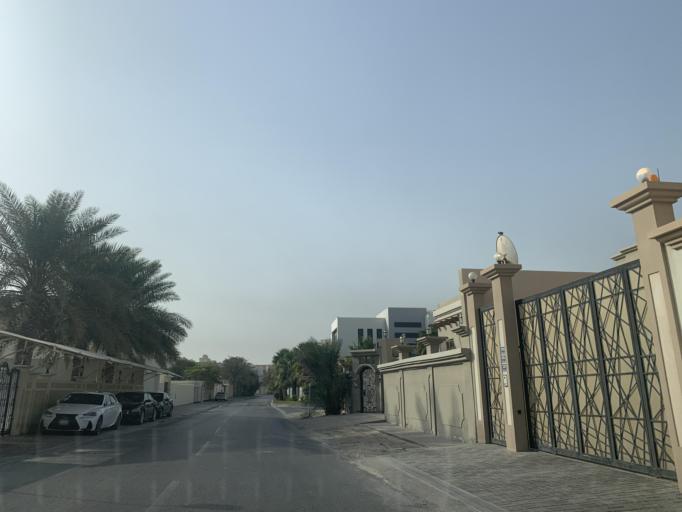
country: BH
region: Northern
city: Madinat `Isa
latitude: 26.1941
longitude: 50.5598
